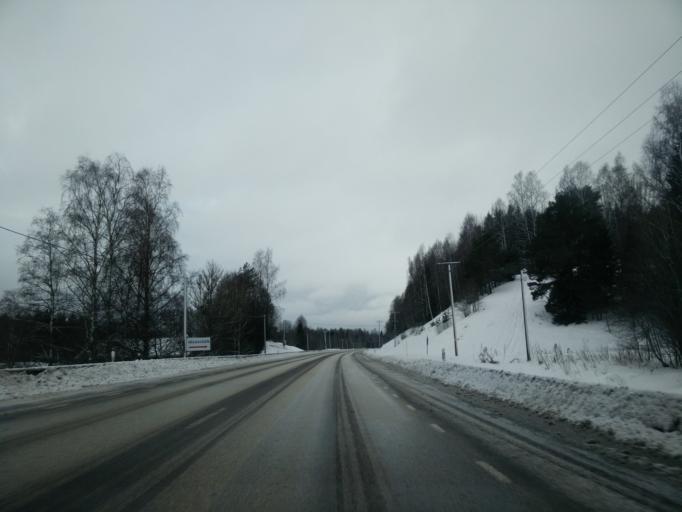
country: SE
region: Vaesternorrland
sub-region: Sundsvalls Kommun
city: Matfors
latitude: 62.3830
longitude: 16.8149
